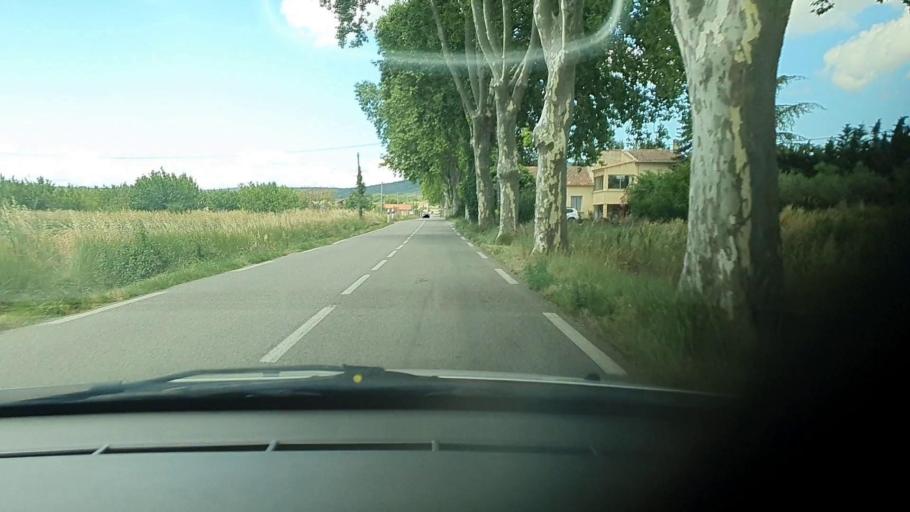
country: FR
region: Languedoc-Roussillon
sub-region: Departement du Gard
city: Saint-Chaptes
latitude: 44.0496
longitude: 4.2900
